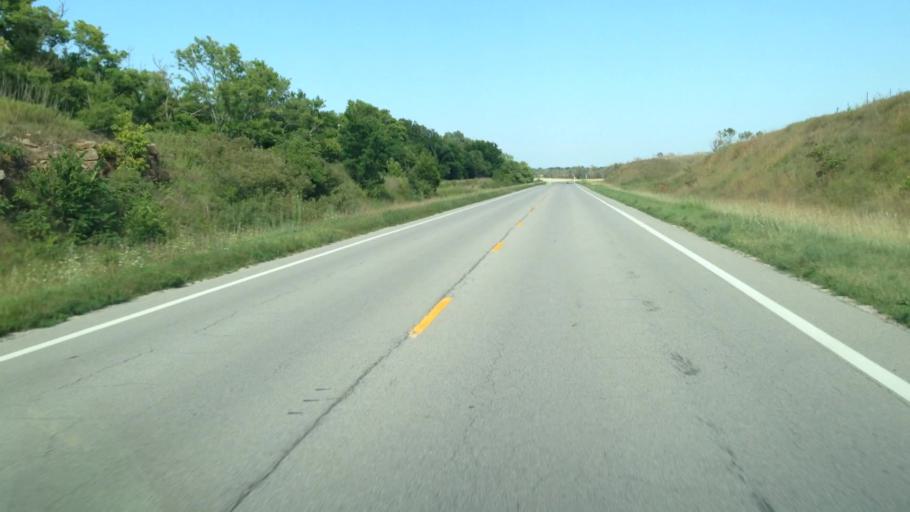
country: US
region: Kansas
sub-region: Neosho County
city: Erie
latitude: 37.6887
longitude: -95.1737
